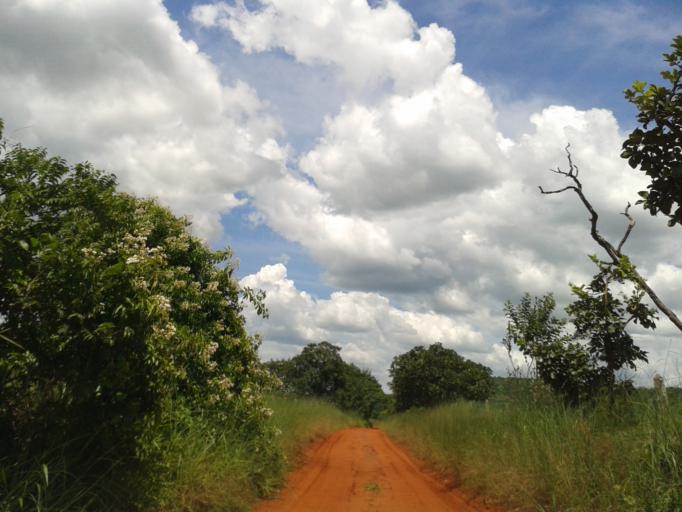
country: BR
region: Minas Gerais
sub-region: Ituiutaba
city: Ituiutaba
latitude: -18.8478
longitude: -49.5065
